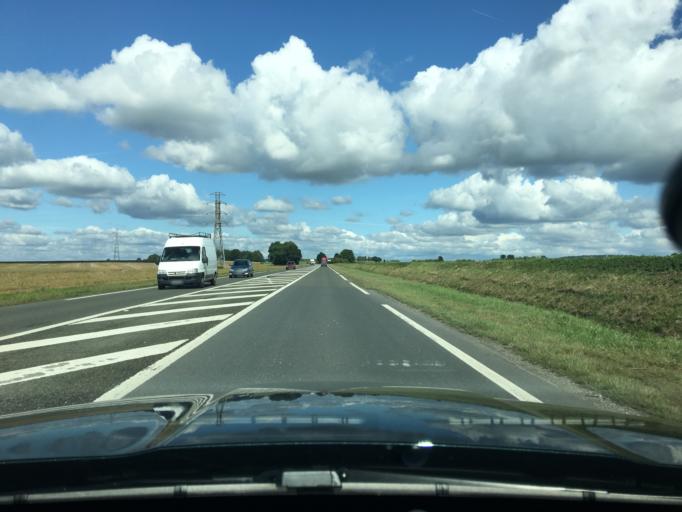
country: FR
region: Ile-de-France
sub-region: Departement du Val-d'Oise
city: Puiseux-en-France
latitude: 49.0656
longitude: 2.5254
